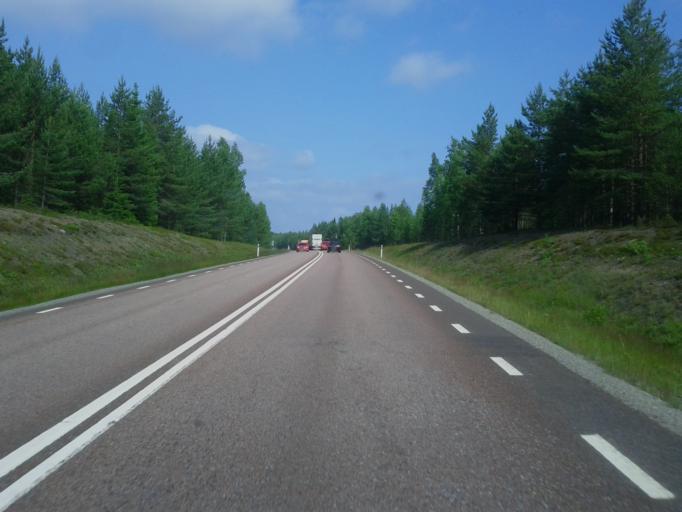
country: SE
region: Vaesterbotten
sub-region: Skelleftea Kommun
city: Burea
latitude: 64.6261
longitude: 21.1784
